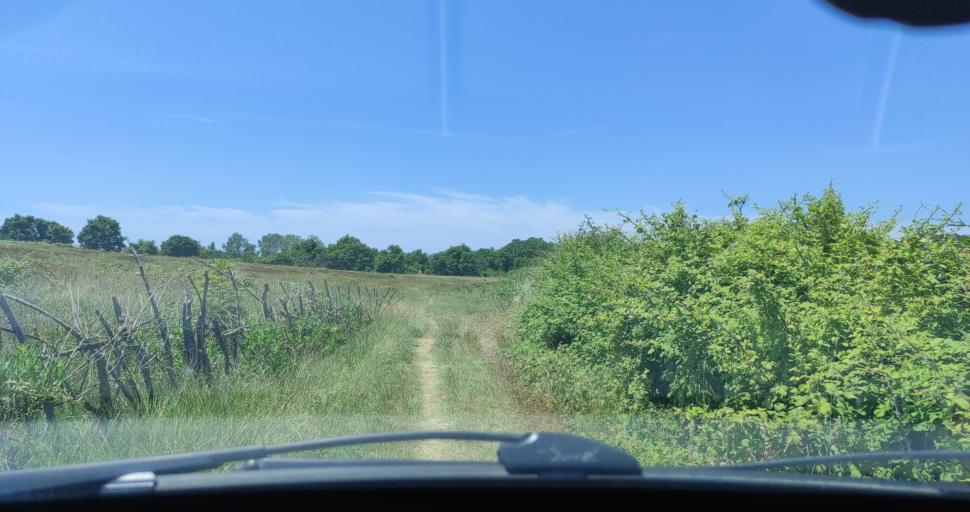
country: AL
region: Shkoder
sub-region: Rrethi i Shkodres
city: Velipoje
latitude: 41.8844
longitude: 19.3871
